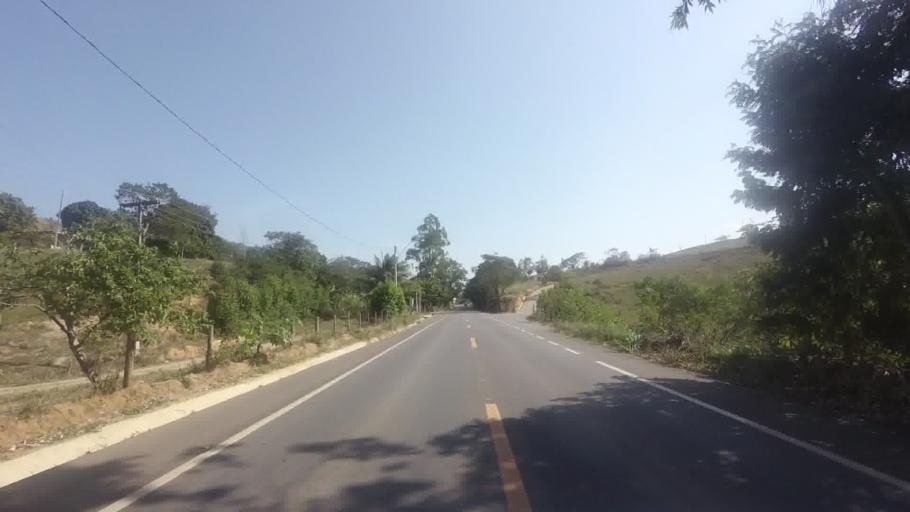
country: BR
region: Espirito Santo
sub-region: Piuma
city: Piuma
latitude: -20.8135
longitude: -40.6858
